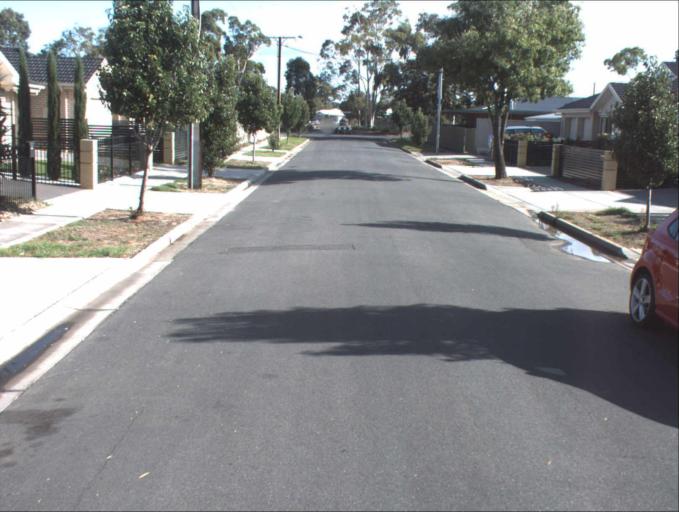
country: AU
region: South Australia
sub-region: Charles Sturt
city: Woodville North
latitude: -34.8571
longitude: 138.5556
